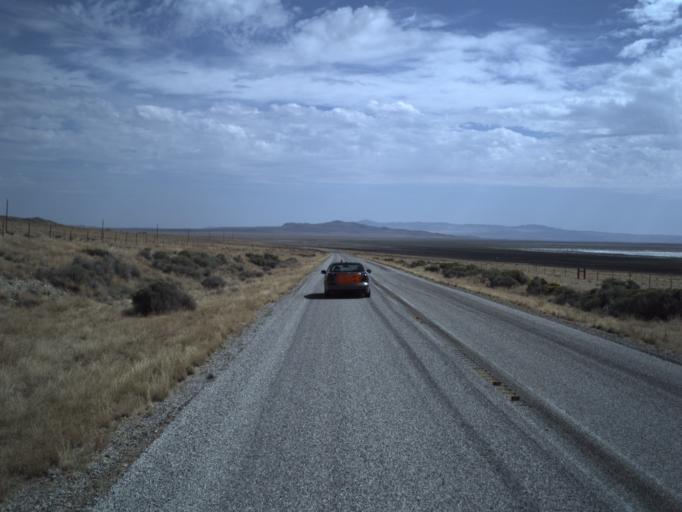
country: US
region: Utah
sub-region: Tooele County
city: Wendover
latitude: 41.4410
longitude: -113.7036
